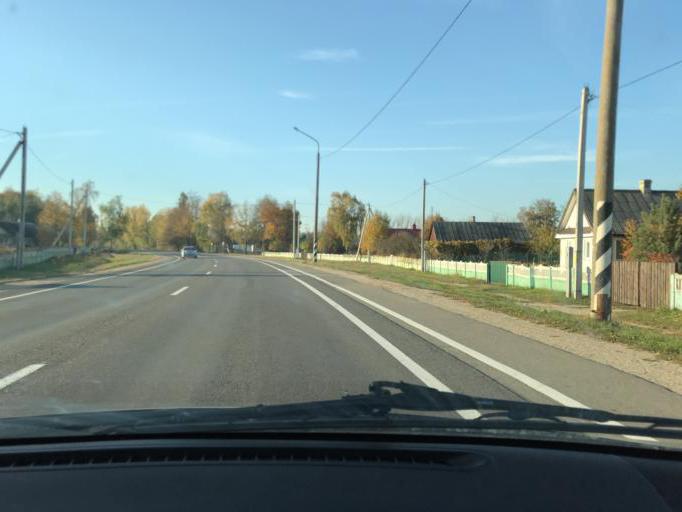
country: BY
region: Brest
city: Horad Kobryn
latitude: 52.2155
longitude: 24.5539
